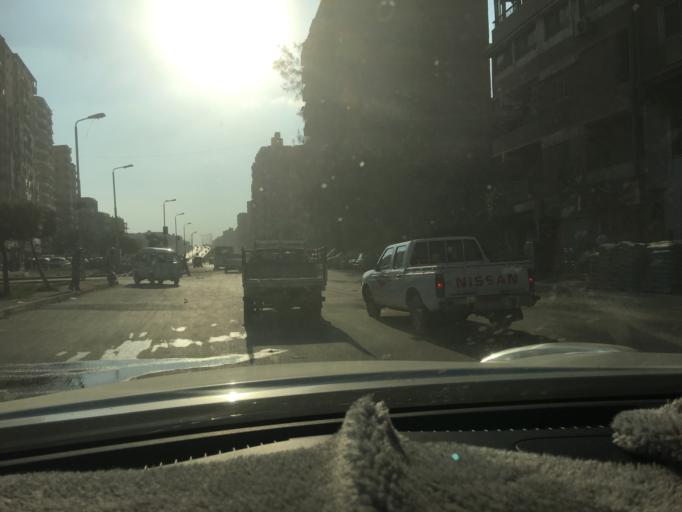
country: EG
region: Muhafazat al Qalyubiyah
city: Al Khankah
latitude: 30.1418
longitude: 31.3348
